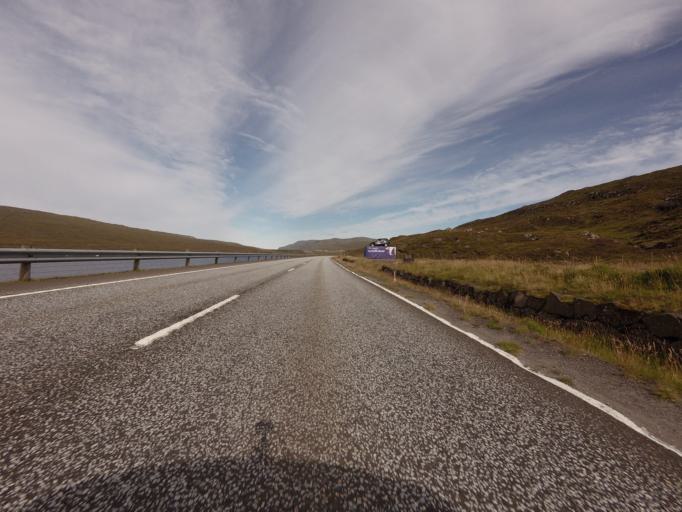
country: FO
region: Vagar
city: Midvagur
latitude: 62.0522
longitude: -7.2314
